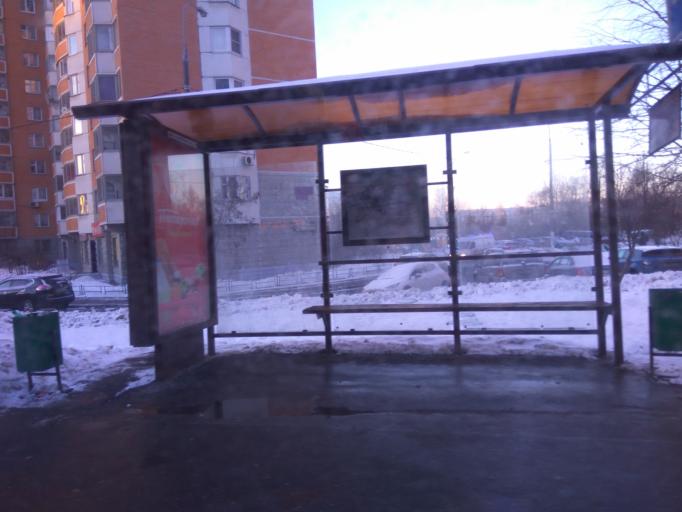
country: RU
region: Moscow
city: Biryulevo
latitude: 55.6018
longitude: 37.6675
